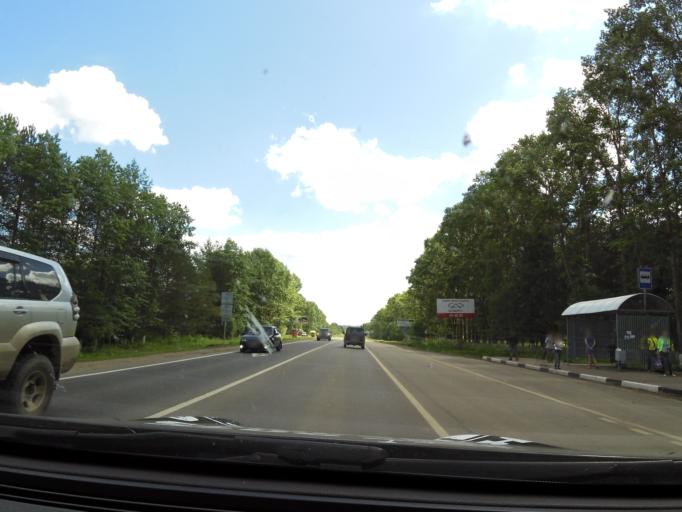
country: RU
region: Vologda
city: Molochnoye
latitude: 59.2600
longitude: 39.7497
